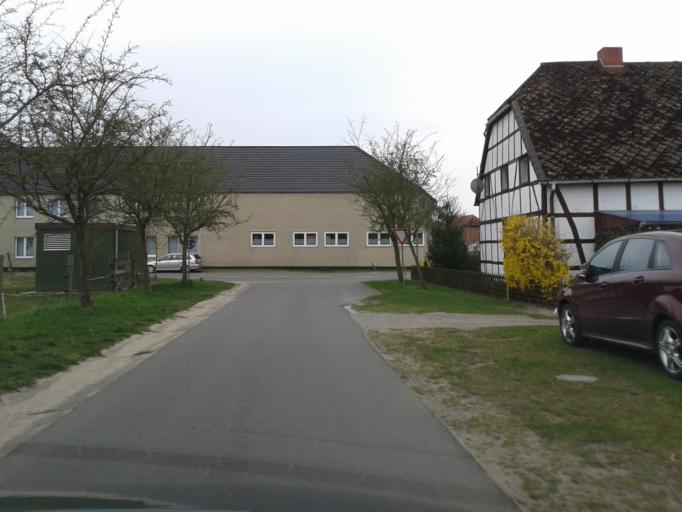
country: DE
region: Lower Saxony
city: Woltersdorf
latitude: 52.9196
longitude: 11.2229
